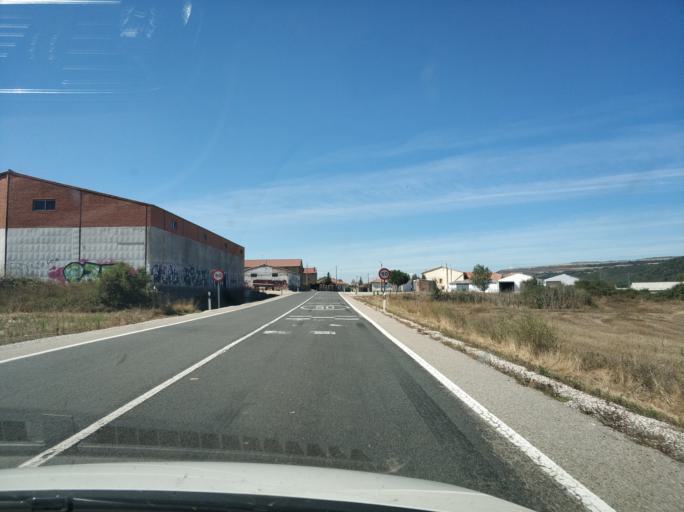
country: ES
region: Castille and Leon
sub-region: Provincia de Burgos
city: Humada
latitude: 42.7285
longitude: -4.0755
